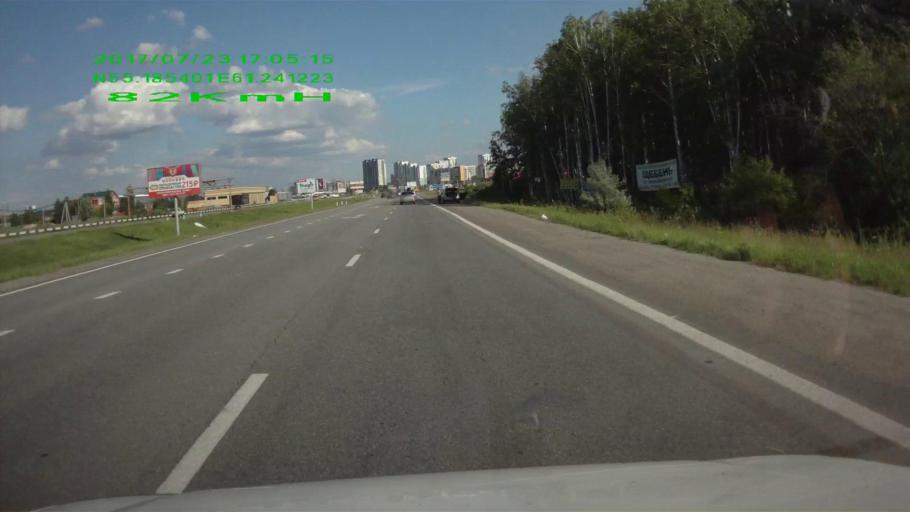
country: RU
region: Chelyabinsk
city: Roshchino
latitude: 55.1841
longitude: 61.2418
